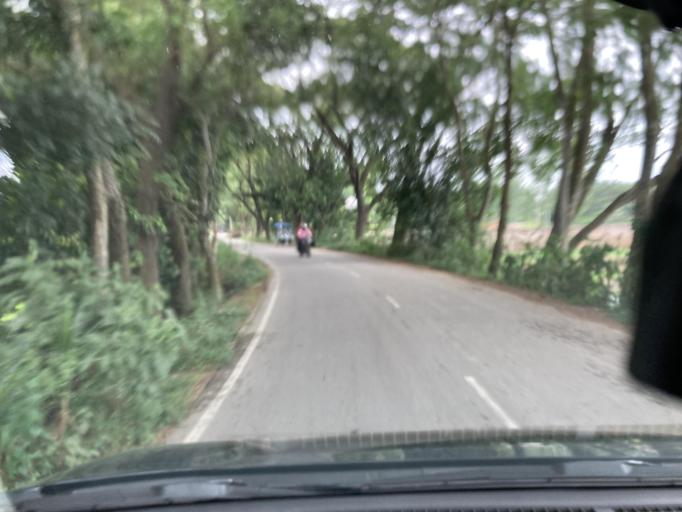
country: BD
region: Dhaka
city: Dohar
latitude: 23.7841
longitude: 90.0655
